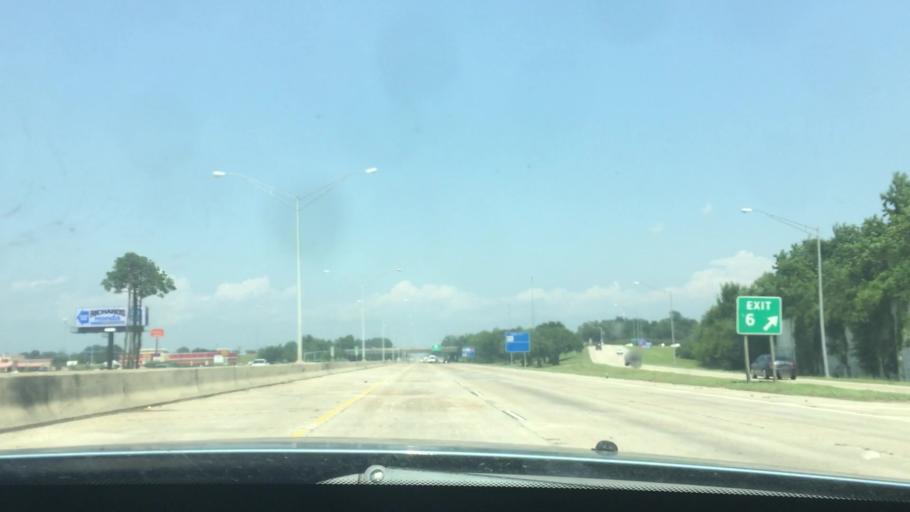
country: US
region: Louisiana
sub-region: East Baton Rouge Parish
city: Shenandoah
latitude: 30.4370
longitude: -91.0289
